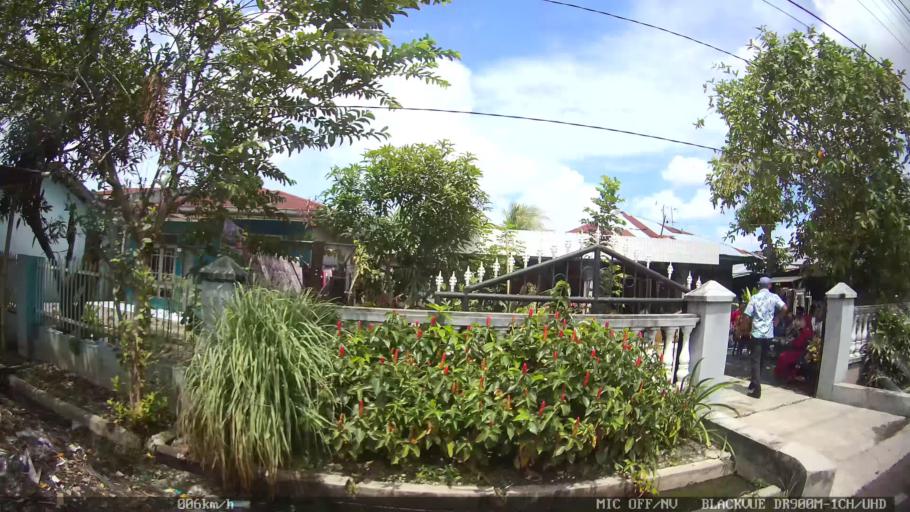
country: ID
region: North Sumatra
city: Percut
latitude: 3.6077
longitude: 98.7815
